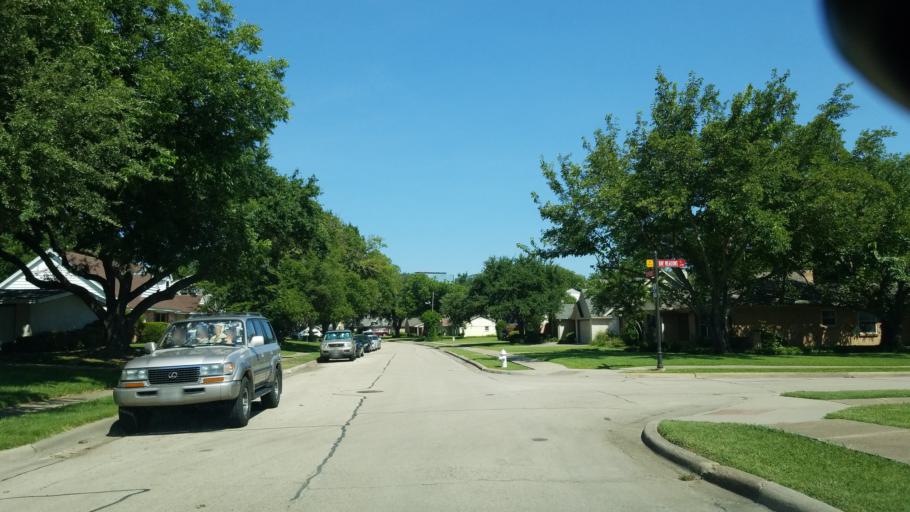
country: US
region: Texas
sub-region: Dallas County
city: Farmers Branch
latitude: 32.9148
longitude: -96.8854
